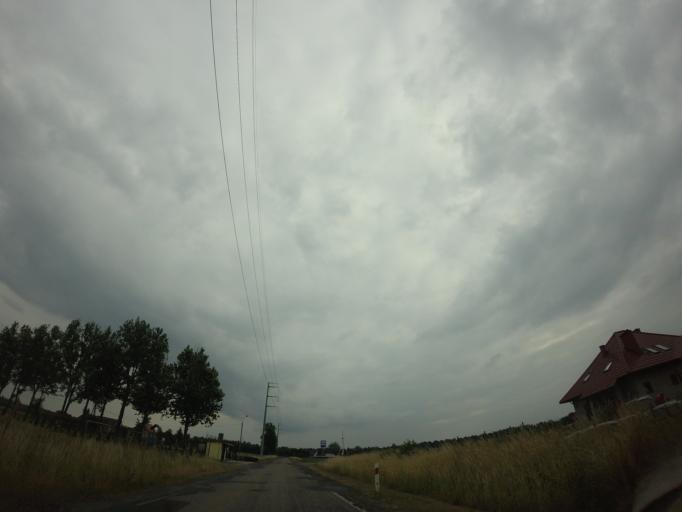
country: PL
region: West Pomeranian Voivodeship
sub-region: Powiat drawski
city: Czaplinek
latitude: 53.5164
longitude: 16.2249
